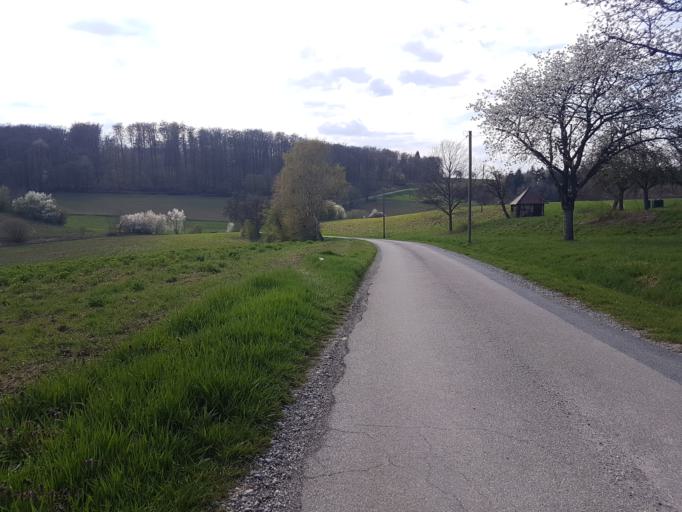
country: DE
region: Baden-Wuerttemberg
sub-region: Regierungsbezirk Stuttgart
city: Forchtenberg
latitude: 49.3300
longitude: 9.5368
